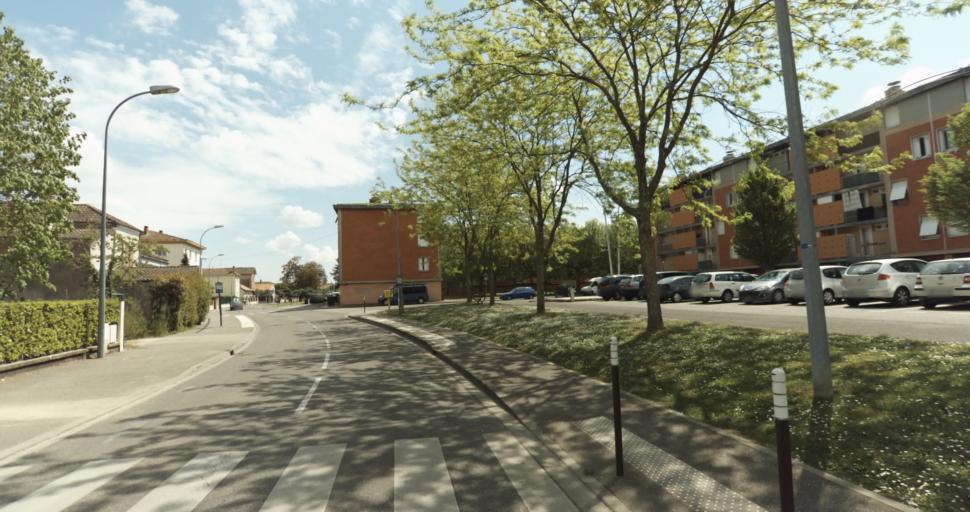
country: FR
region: Aquitaine
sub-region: Departement du Lot-et-Garonne
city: Agen
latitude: 44.1979
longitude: 0.6324
